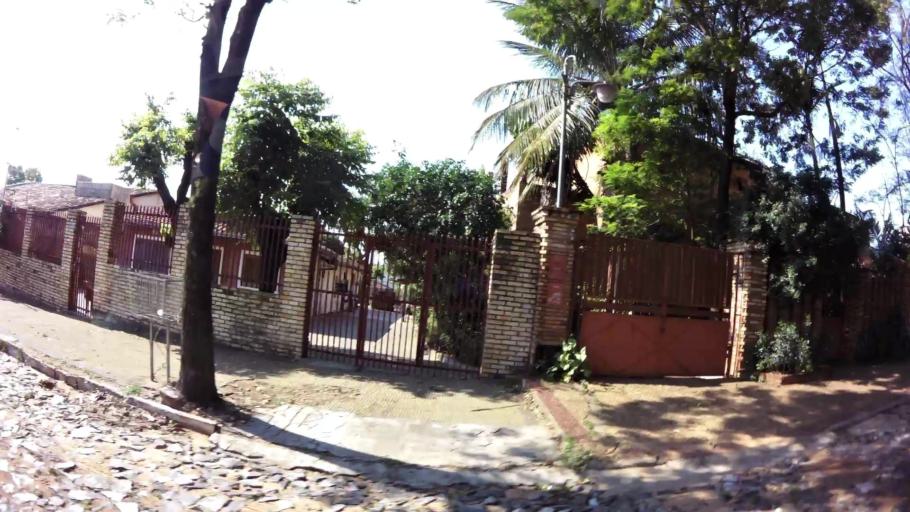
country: PY
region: Asuncion
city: Asuncion
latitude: -25.3164
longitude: -57.6314
